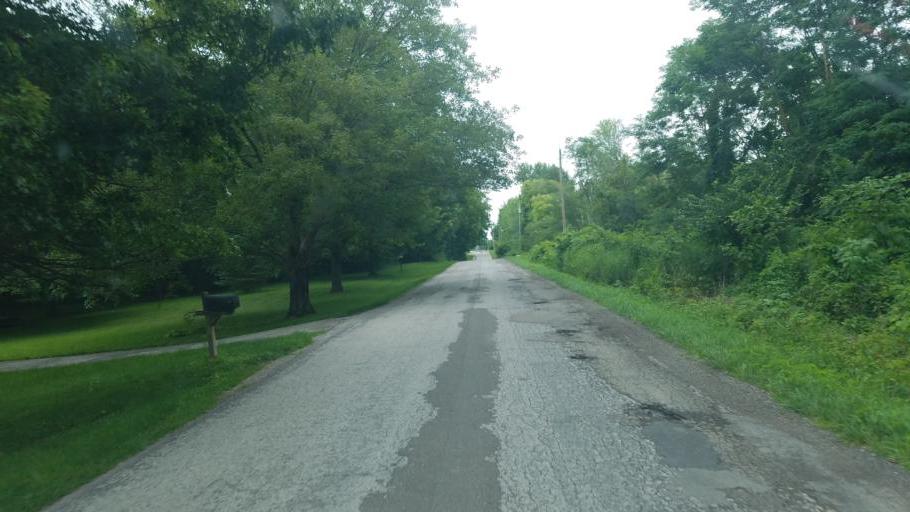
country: US
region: Ohio
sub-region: Delaware County
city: Ashley
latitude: 40.4472
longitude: -82.9610
